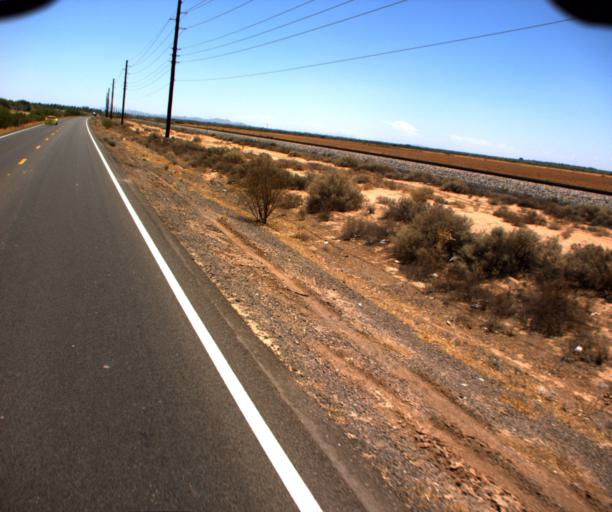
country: US
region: Arizona
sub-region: Pinal County
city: Maricopa
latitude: 33.0792
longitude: -112.1088
